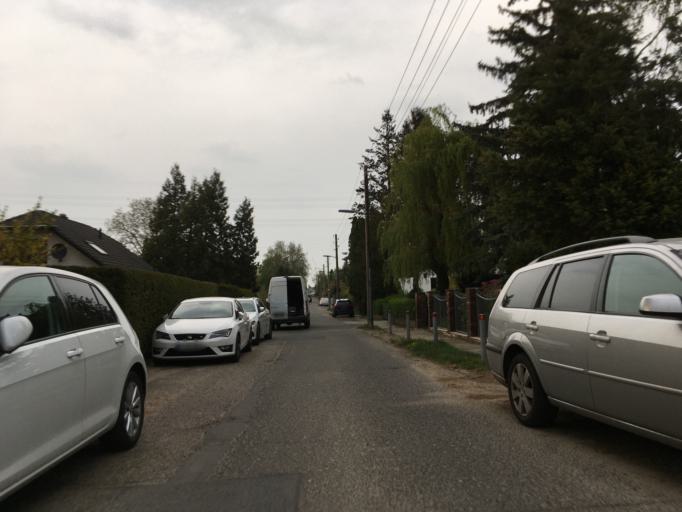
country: DE
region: Berlin
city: Wartenberg
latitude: 52.5891
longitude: 13.5336
